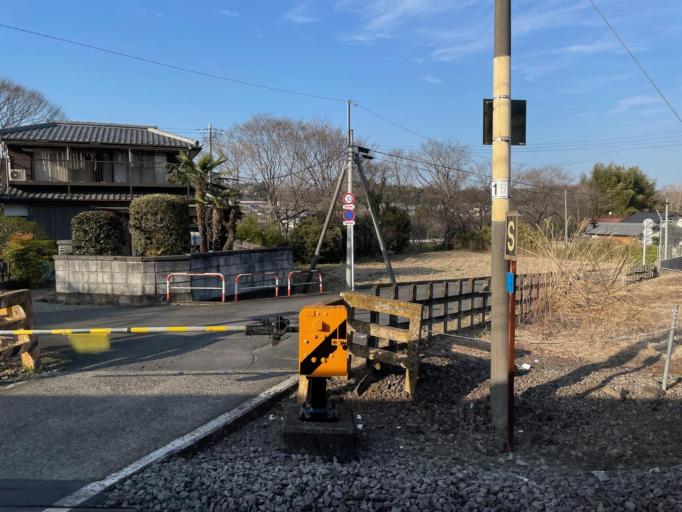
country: JP
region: Gunma
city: Annaka
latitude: 36.3070
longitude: 138.8015
